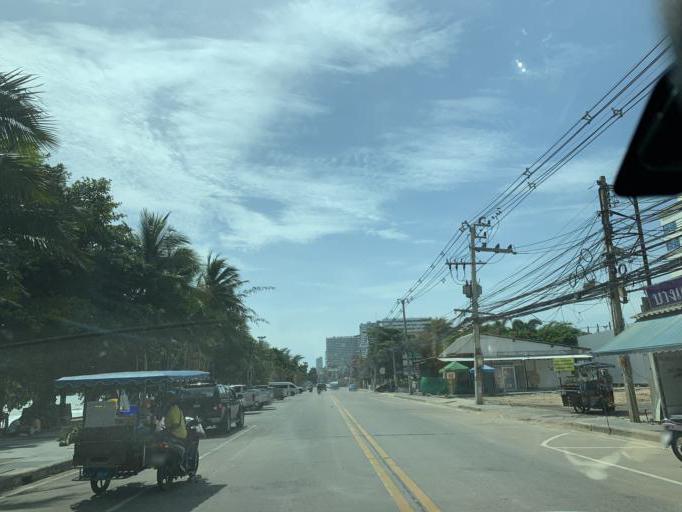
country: TH
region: Chon Buri
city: Phatthaya
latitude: 12.8922
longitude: 100.8730
